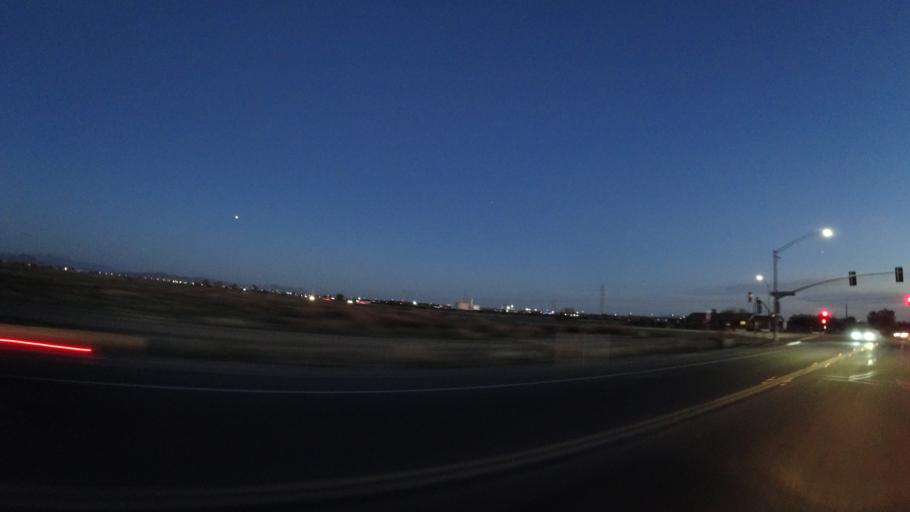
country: US
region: Arizona
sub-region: Maricopa County
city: Tempe
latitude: 33.4517
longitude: -111.8835
